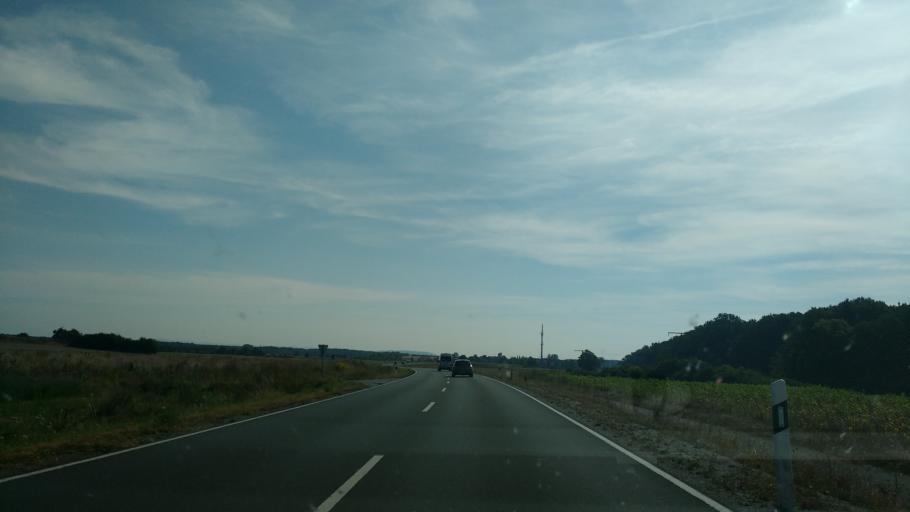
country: DE
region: Bavaria
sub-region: Regierungsbezirk Mittelfranken
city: Grossenseebach
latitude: 49.6315
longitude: 10.8915
